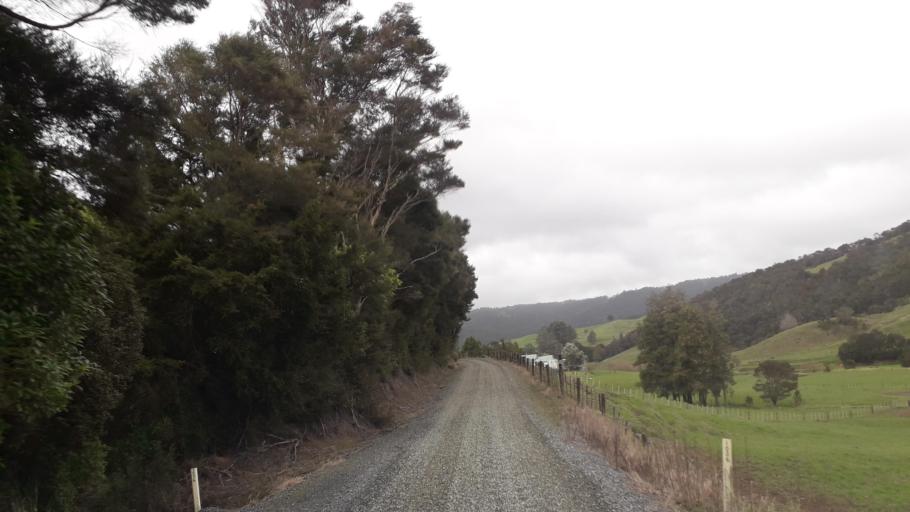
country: NZ
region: Northland
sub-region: Far North District
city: Waimate North
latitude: -35.1444
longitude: 173.7130
